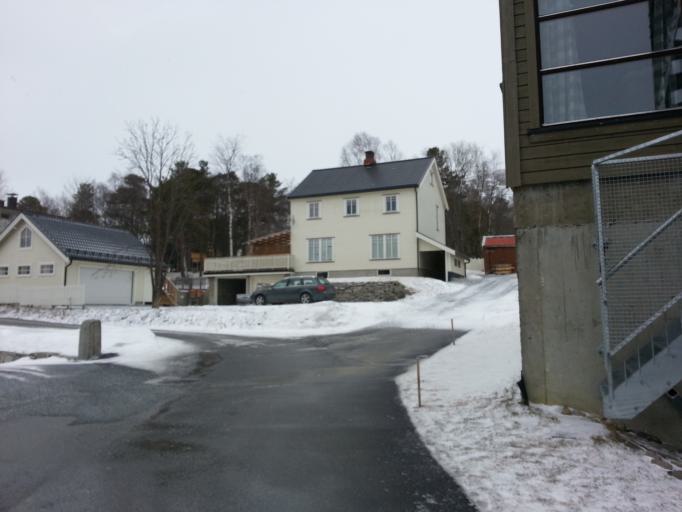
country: NO
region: Sor-Trondelag
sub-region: Oppdal
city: Oppdal
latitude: 62.5959
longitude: 9.6944
